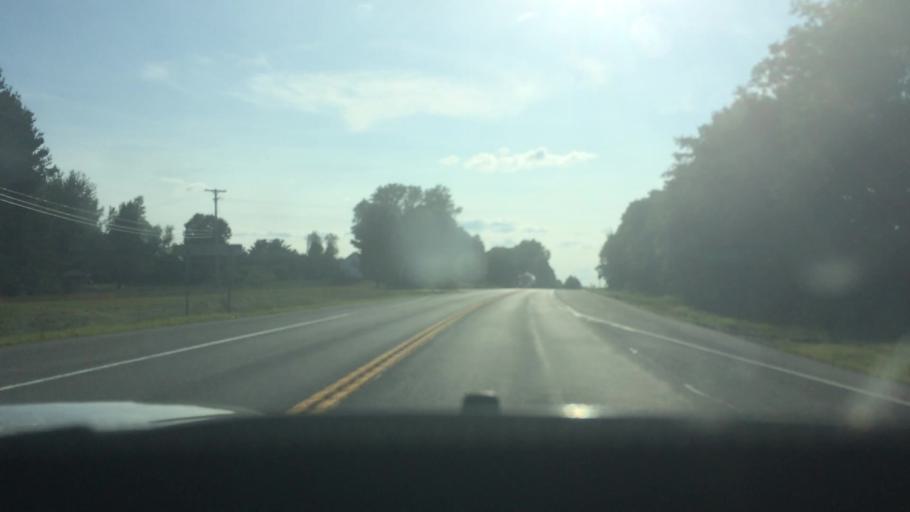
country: US
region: New York
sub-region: St. Lawrence County
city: Potsdam
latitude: 44.6739
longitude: -74.8522
